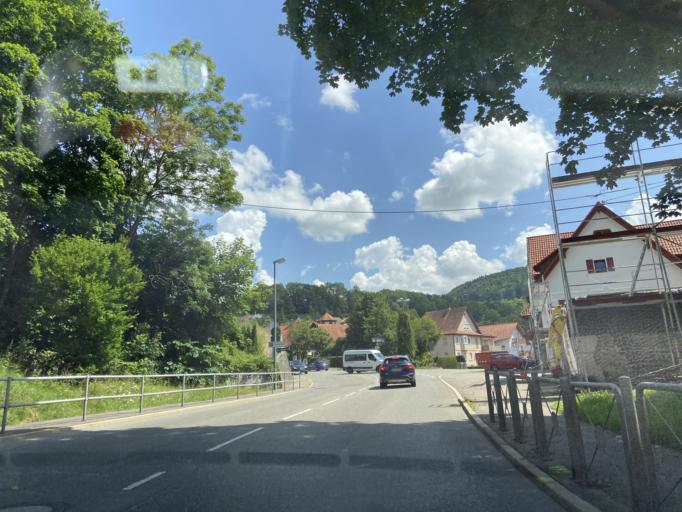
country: DE
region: Baden-Wuerttemberg
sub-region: Tuebingen Region
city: Messstetten
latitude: 48.2151
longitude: 8.9617
